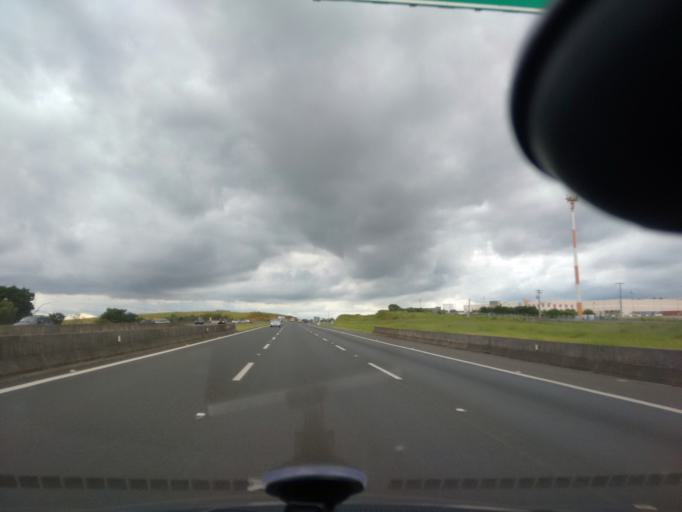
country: BR
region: Sao Paulo
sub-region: Hortolandia
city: Hortolandia
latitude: -22.9123
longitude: -47.1820
